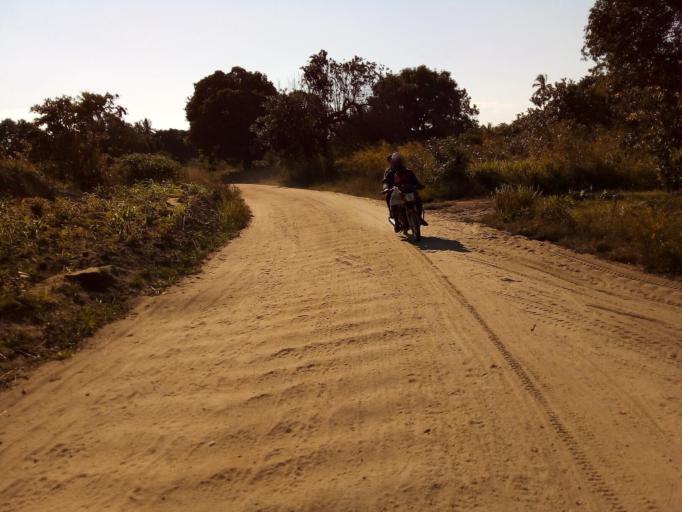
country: MZ
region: Zambezia
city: Quelimane
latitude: -17.5250
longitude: 36.6162
